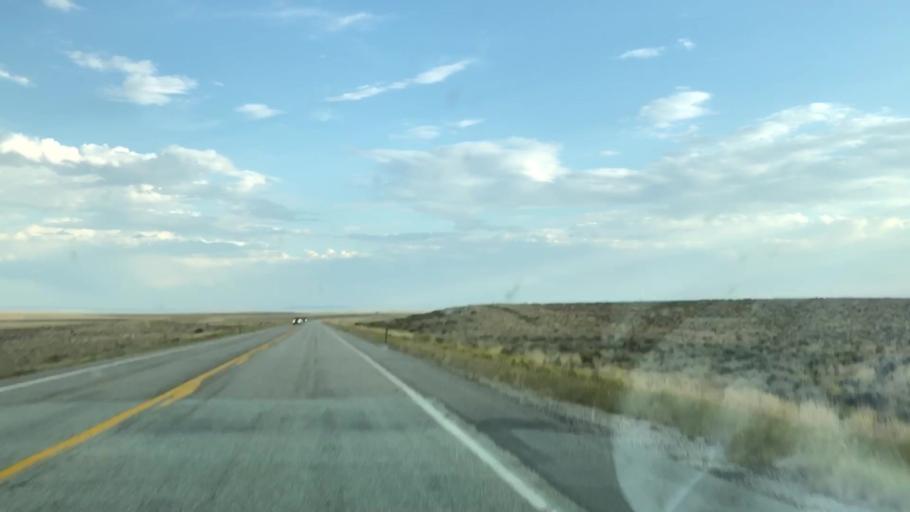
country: US
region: Wyoming
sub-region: Sweetwater County
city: North Rock Springs
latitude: 42.2612
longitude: -109.4724
